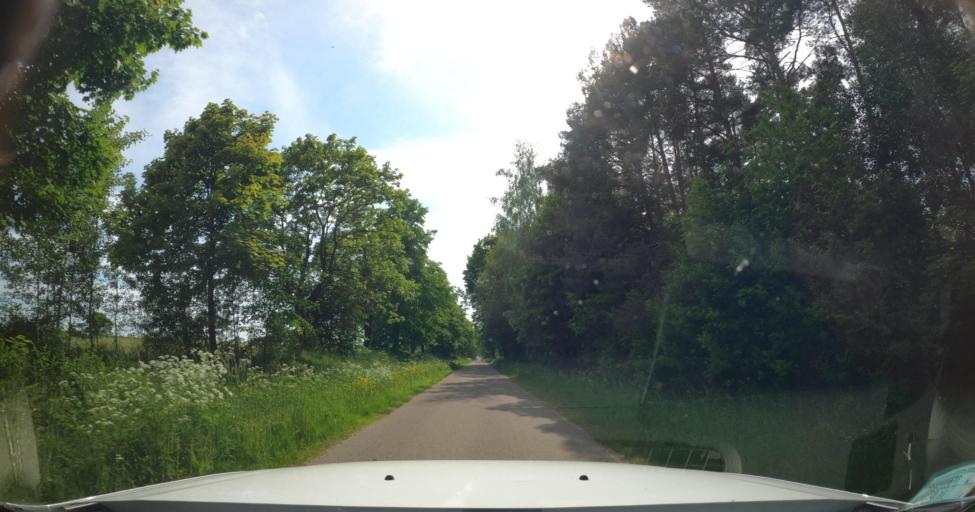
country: PL
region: Warmian-Masurian Voivodeship
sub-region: Powiat lidzbarski
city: Lubomino
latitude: 54.0975
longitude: 20.3149
